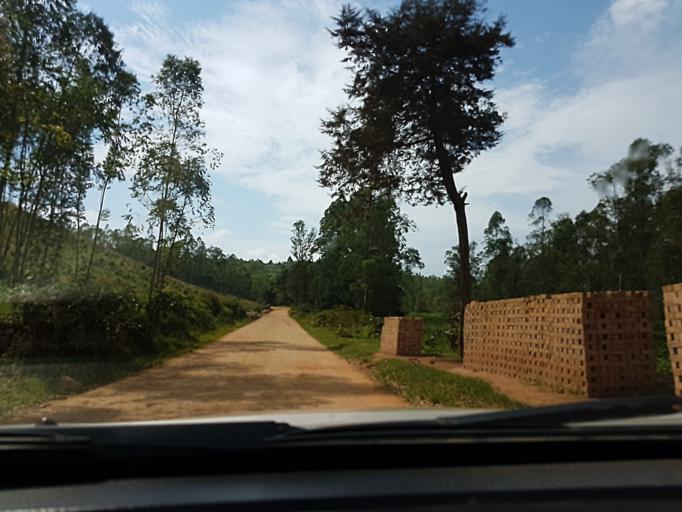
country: CD
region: South Kivu
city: Bukavu
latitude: -2.6404
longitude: 28.8754
